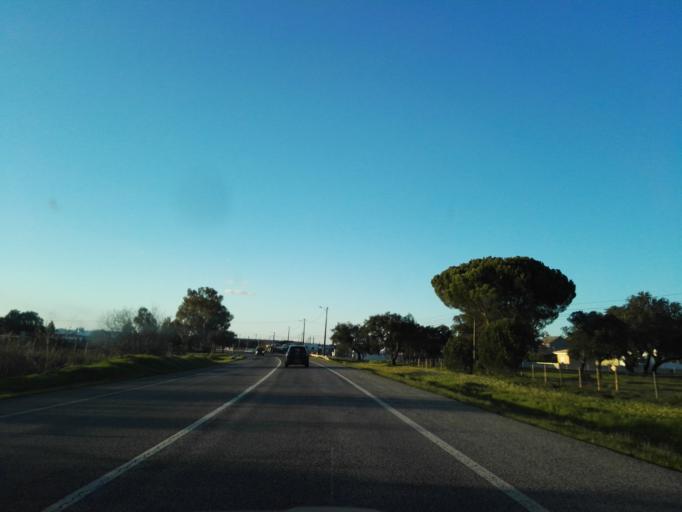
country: PT
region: Santarem
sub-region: Benavente
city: Samora Correia
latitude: 38.9090
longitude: -8.8463
